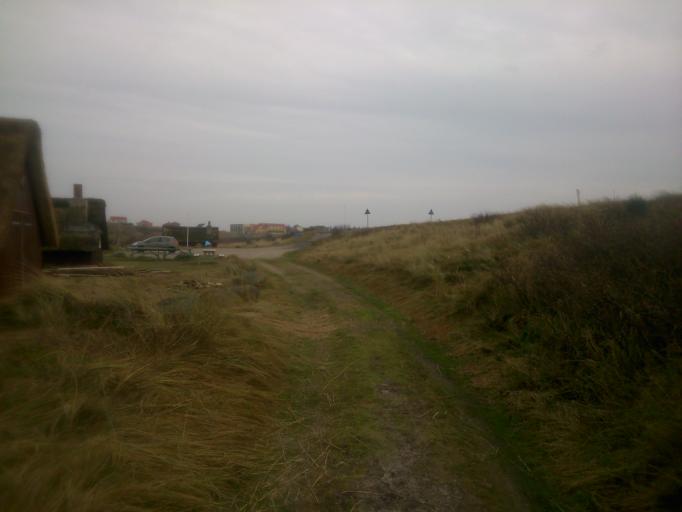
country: DK
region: Central Jutland
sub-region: Ringkobing-Skjern Kommune
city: Hvide Sande
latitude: 55.8188
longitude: 8.1837
